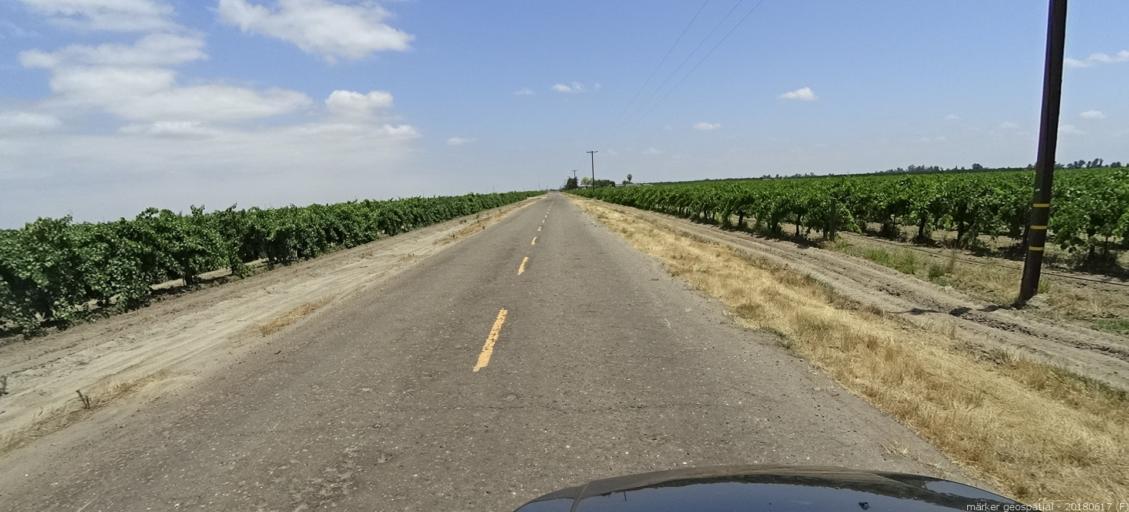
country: US
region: California
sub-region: Fresno County
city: Biola
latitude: 36.8222
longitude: -120.1304
